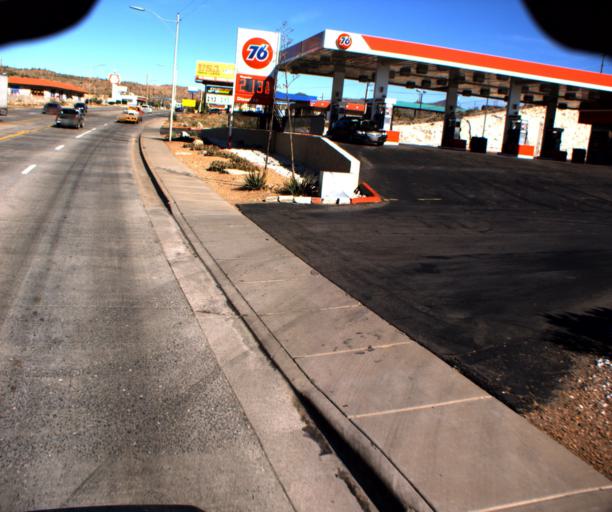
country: US
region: Arizona
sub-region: Mohave County
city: Kingman
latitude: 35.1915
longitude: -114.0692
